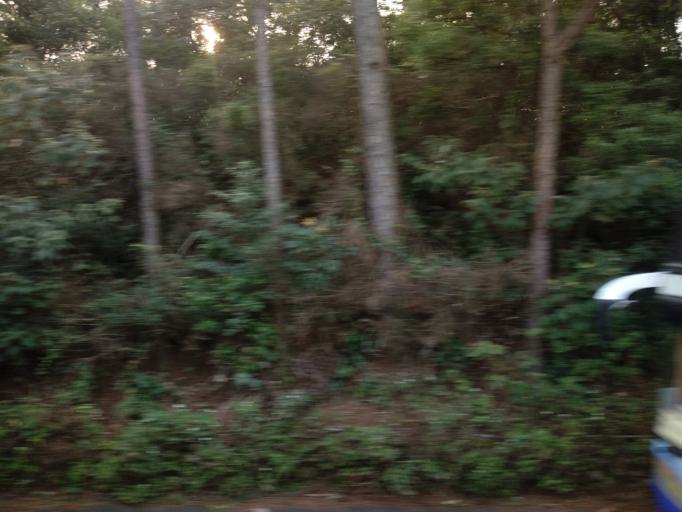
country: TW
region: Taiwan
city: Daxi
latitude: 24.8239
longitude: 121.1830
